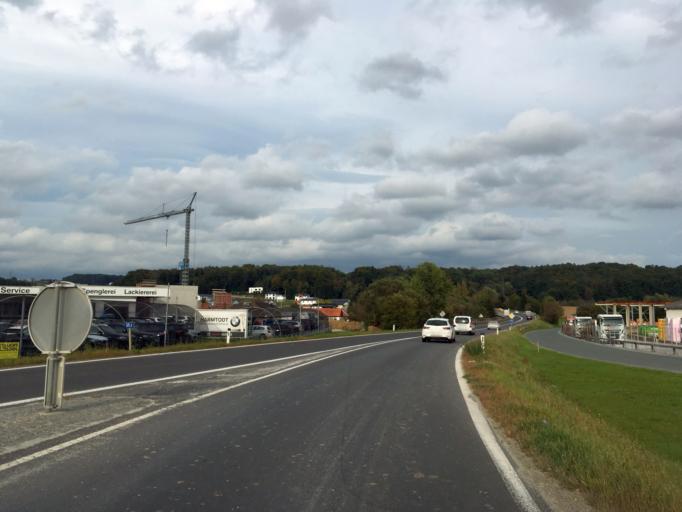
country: AT
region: Styria
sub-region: Politischer Bezirk Hartberg-Fuerstenfeld
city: Grafendorf bei Hartberg
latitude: 47.3353
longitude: 15.9914
